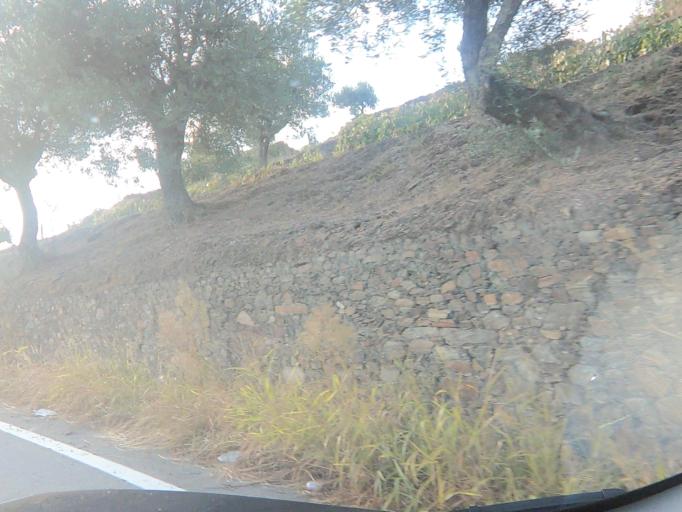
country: PT
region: Vila Real
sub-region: Peso da Regua
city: Peso da Regua
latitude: 41.1748
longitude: -7.7764
